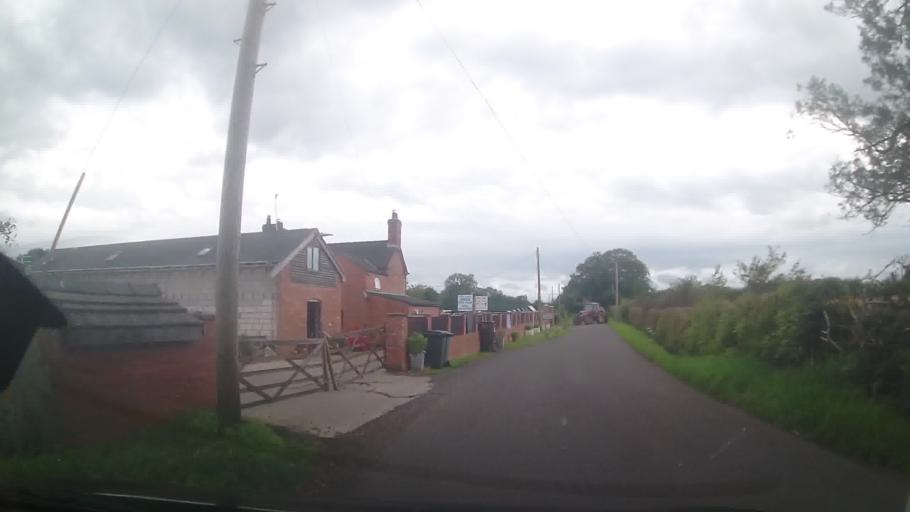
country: GB
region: England
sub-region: Shropshire
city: Whitchurch
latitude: 52.9255
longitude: -2.7295
